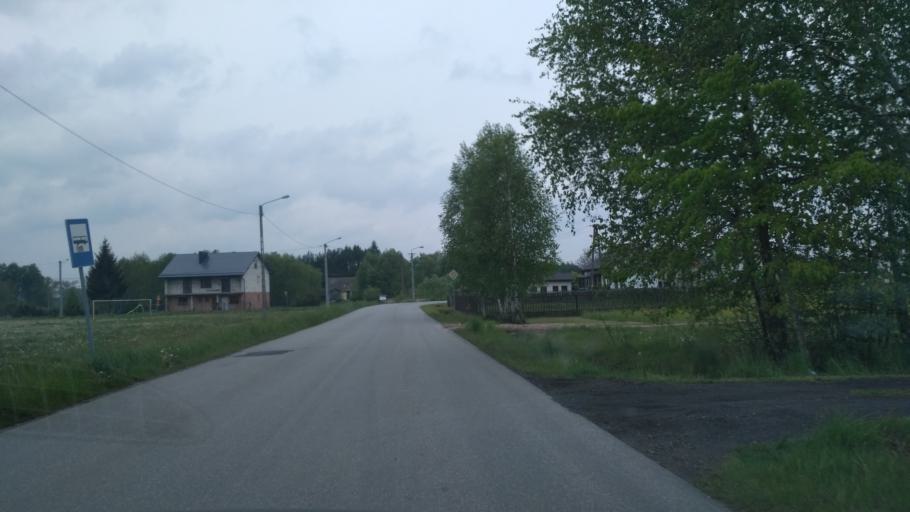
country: PL
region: Subcarpathian Voivodeship
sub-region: Powiat kolbuszowski
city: Kolbuszowa
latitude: 50.1964
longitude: 21.8142
